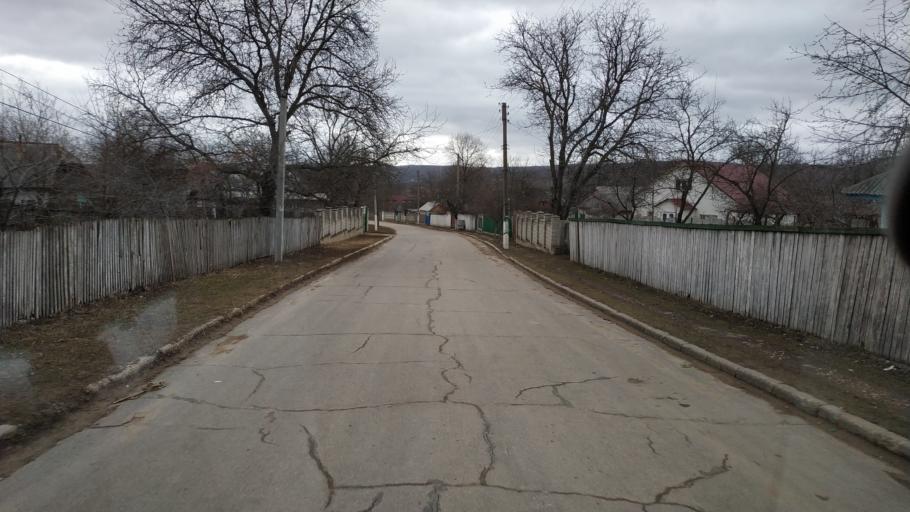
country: MD
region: Calarasi
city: Calarasi
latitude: 47.2639
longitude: 28.1325
